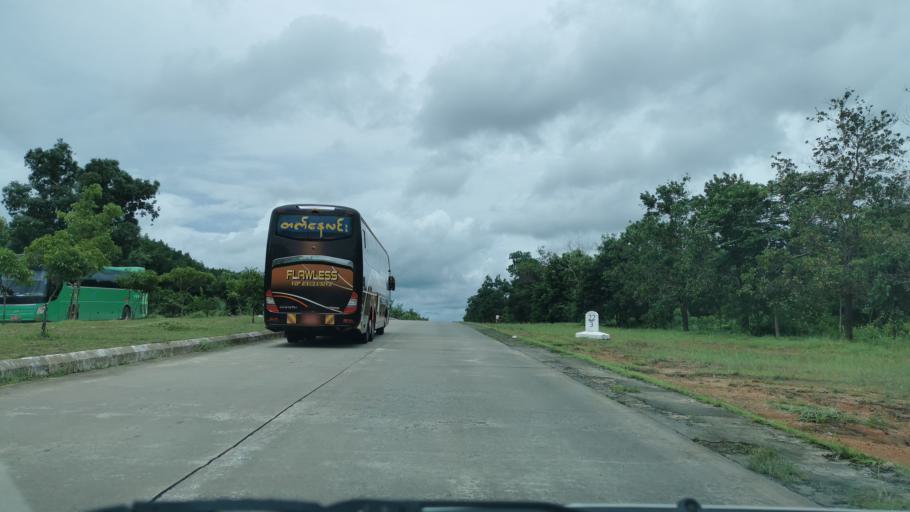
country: MM
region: Bago
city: Thanatpin
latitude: 17.3499
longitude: 96.2361
